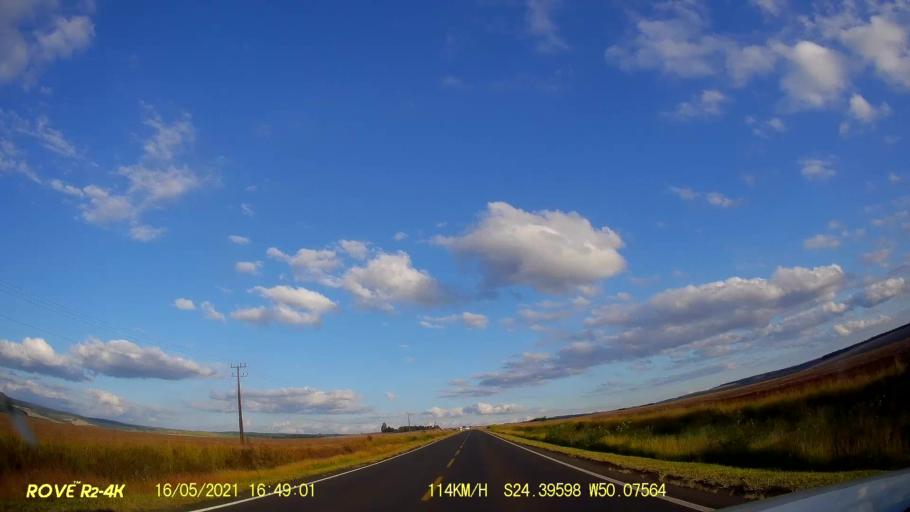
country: BR
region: Parana
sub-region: Pirai Do Sul
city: Pirai do Sul
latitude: -24.3963
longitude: -50.0758
